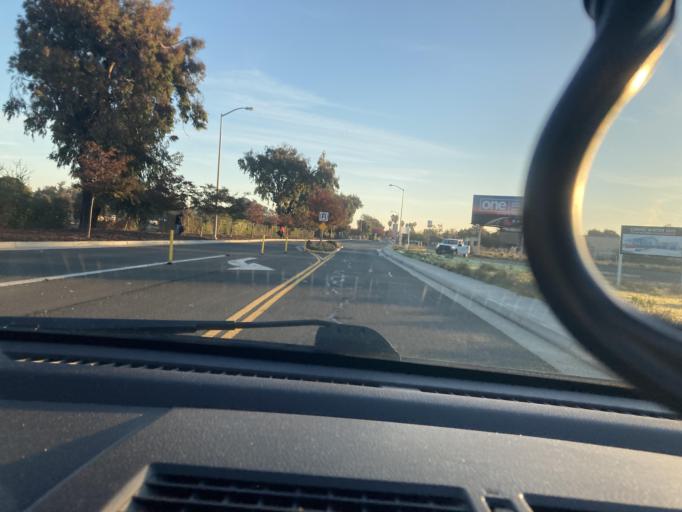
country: US
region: California
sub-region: Solano County
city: Fairfield
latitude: 38.2461
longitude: -122.0765
